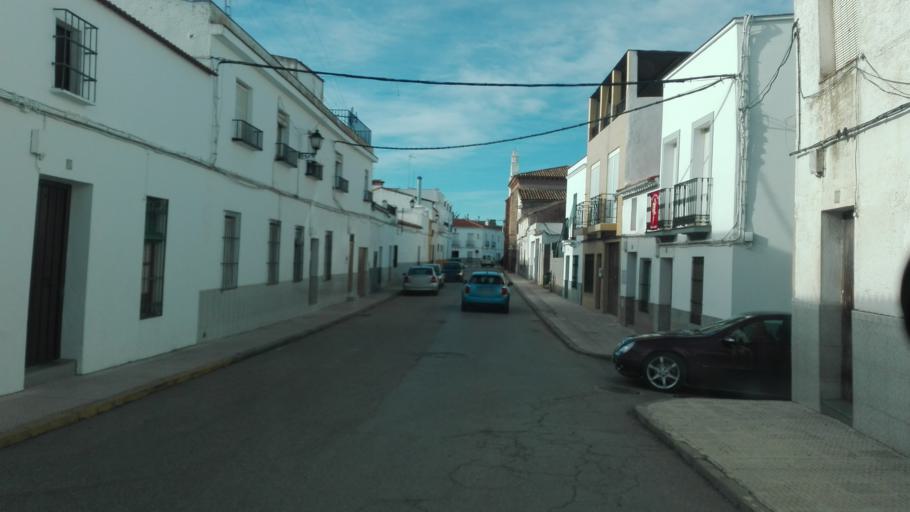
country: ES
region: Extremadura
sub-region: Provincia de Badajoz
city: Usagre
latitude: 38.3562
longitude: -6.1680
